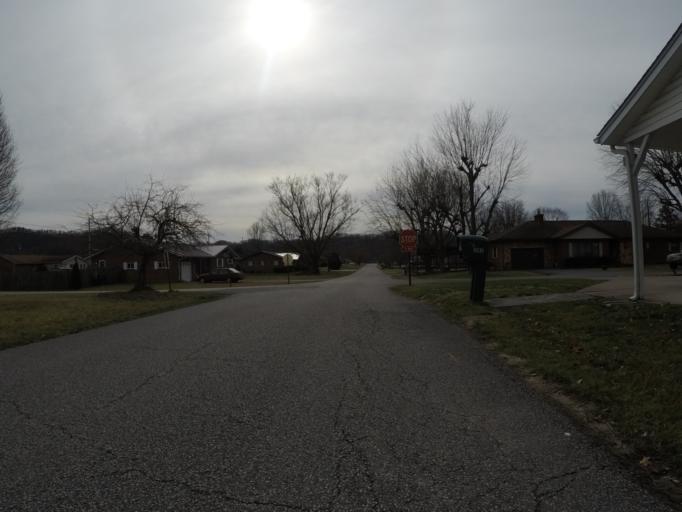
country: US
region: West Virginia
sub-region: Cabell County
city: Pea Ridge
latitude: 38.4484
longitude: -82.3390
